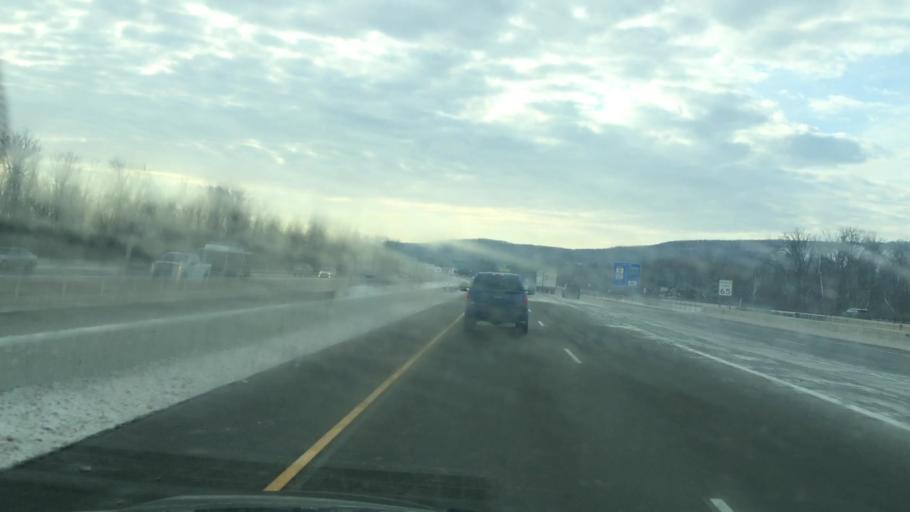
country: US
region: Wisconsin
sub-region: Marathon County
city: Rib Mountain
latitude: 44.9452
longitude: -89.6667
